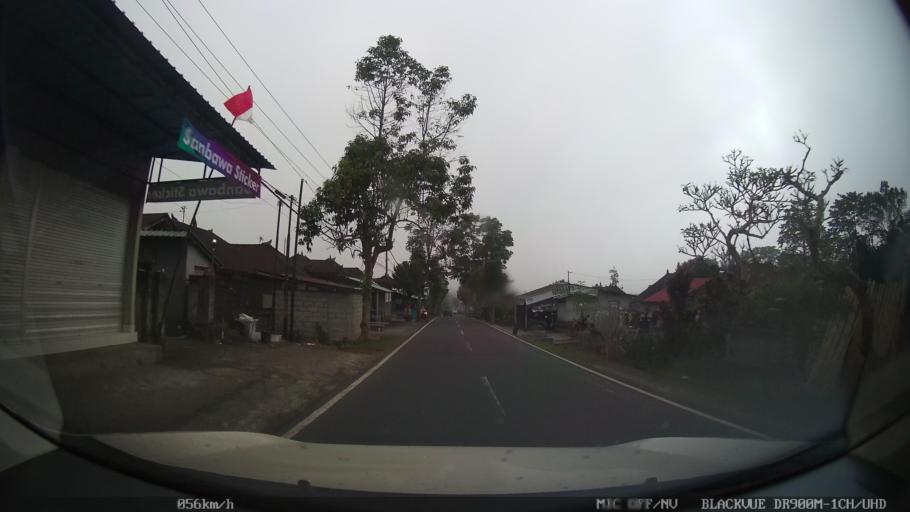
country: ID
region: Bali
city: Banjar Kedisan
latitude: -8.3042
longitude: 115.3073
